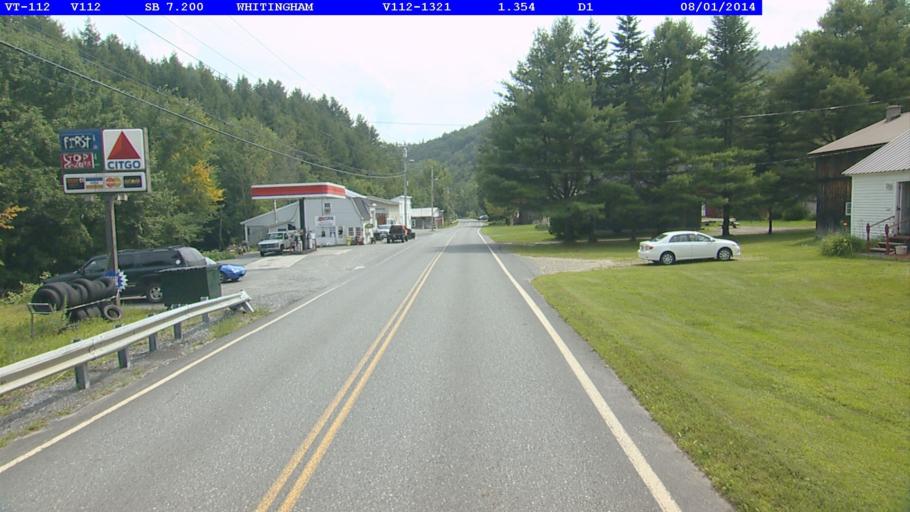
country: US
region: Vermont
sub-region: Windham County
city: Dover
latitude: 42.7936
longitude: -72.8204
